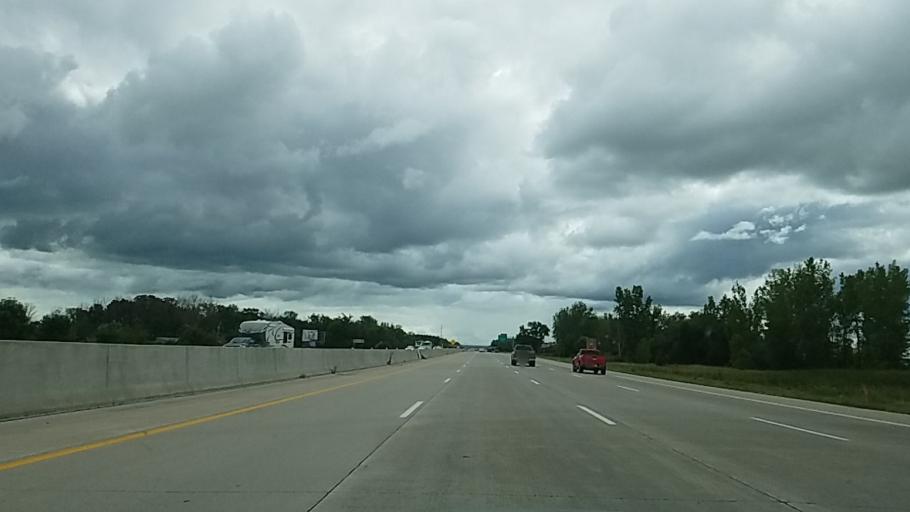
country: US
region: Michigan
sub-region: Saginaw County
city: Zilwaukee
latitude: 43.5193
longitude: -83.9387
